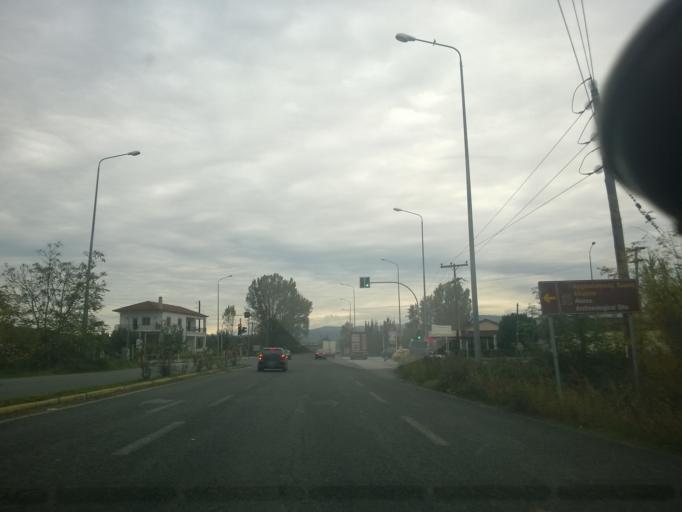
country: GR
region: Central Macedonia
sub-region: Nomos Pellis
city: Apsalos
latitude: 40.9288
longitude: 22.0841
